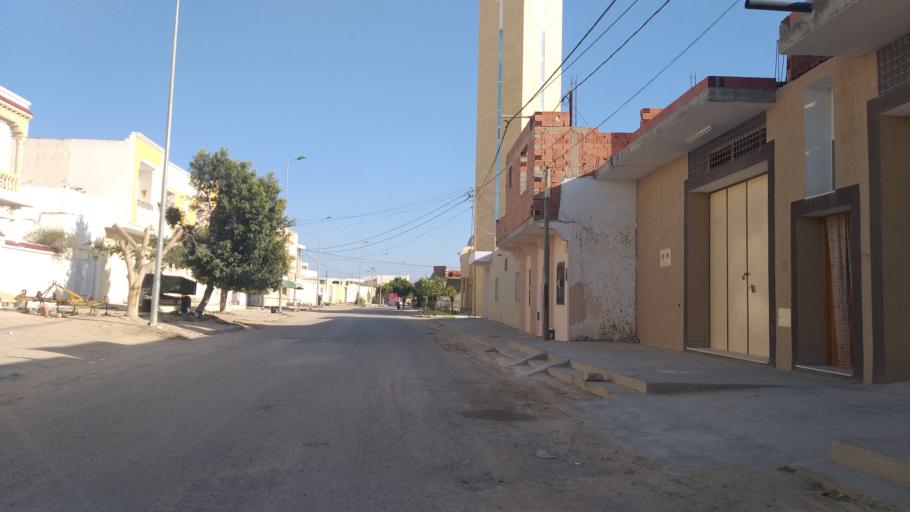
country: TN
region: Al Mahdiyah
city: El Jem
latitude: 35.2883
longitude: 10.7085
